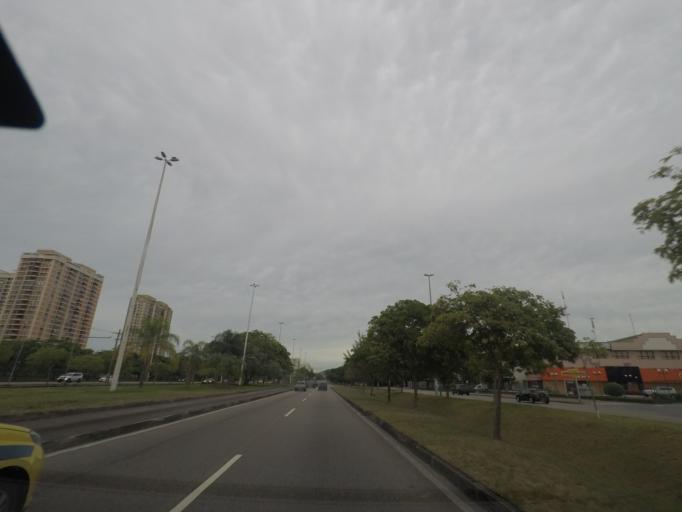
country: BR
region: Rio de Janeiro
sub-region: Nilopolis
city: Nilopolis
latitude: -23.0002
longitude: -43.3791
